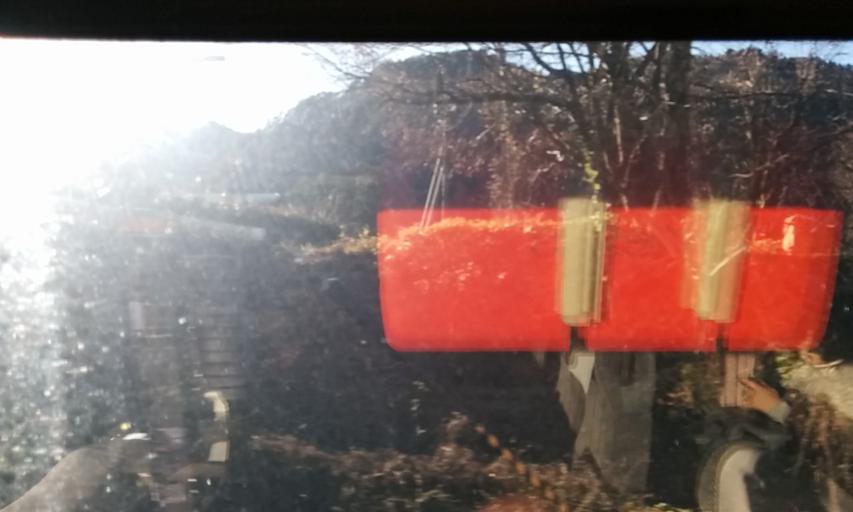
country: JP
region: Nagano
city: Ina
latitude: 35.8128
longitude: 137.6838
